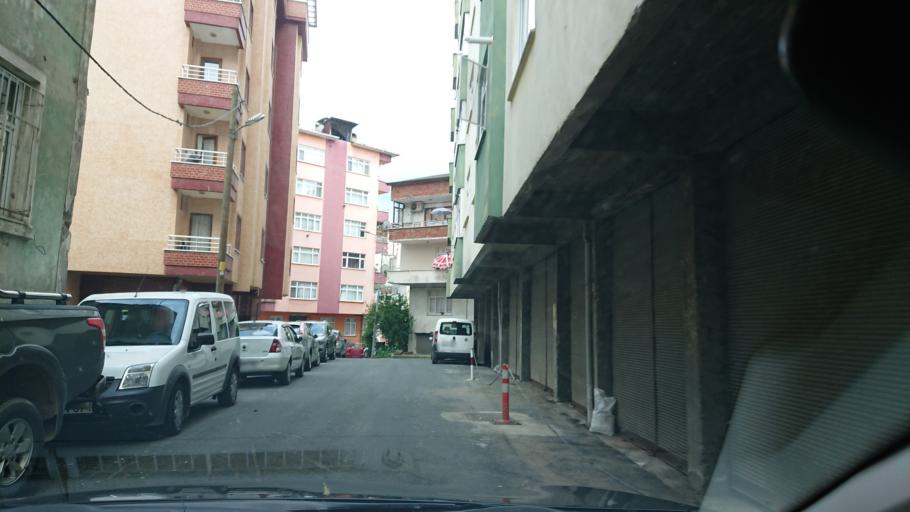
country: TR
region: Rize
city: Rize
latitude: 41.0228
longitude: 40.5173
